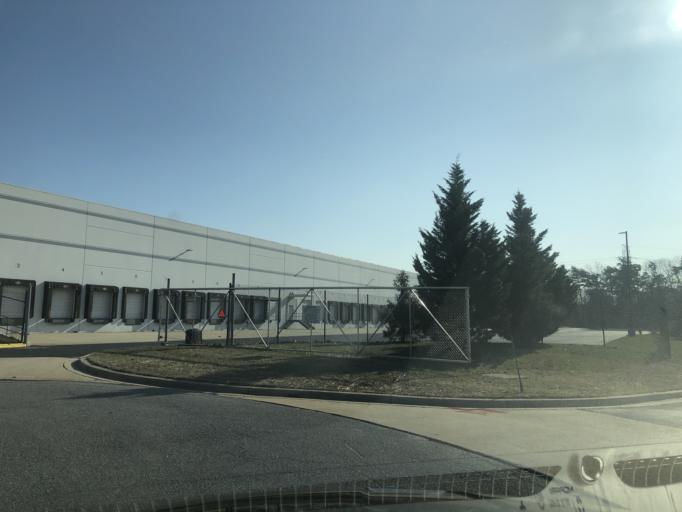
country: US
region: Maryland
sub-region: Anne Arundel County
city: Odenton
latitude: 39.0877
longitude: -76.6879
